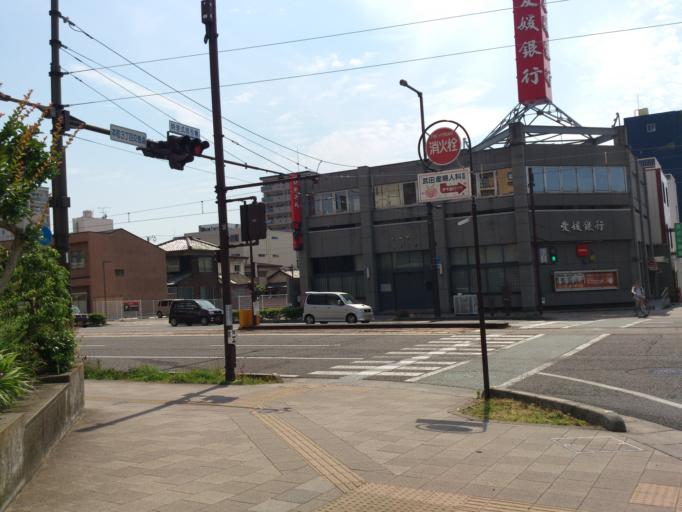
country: JP
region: Ehime
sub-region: Shikoku-chuo Shi
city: Matsuyama
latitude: 33.8476
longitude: 132.7591
